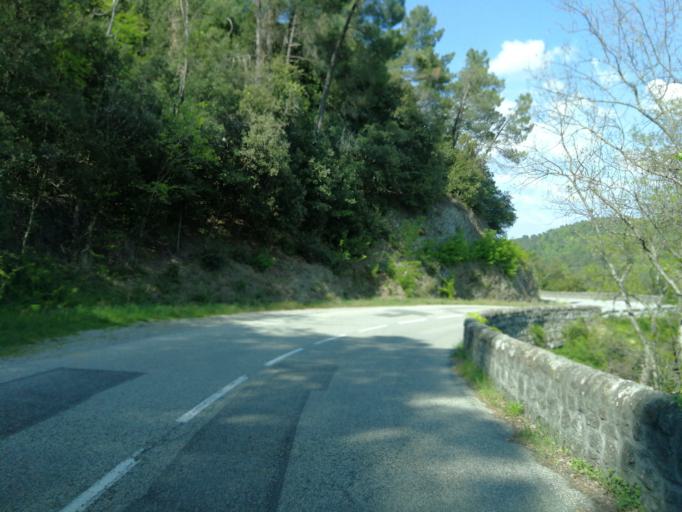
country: FR
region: Rhone-Alpes
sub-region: Departement de l'Ardeche
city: Saint-Sauveur-de-Montagut
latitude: 44.7919
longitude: 4.6122
